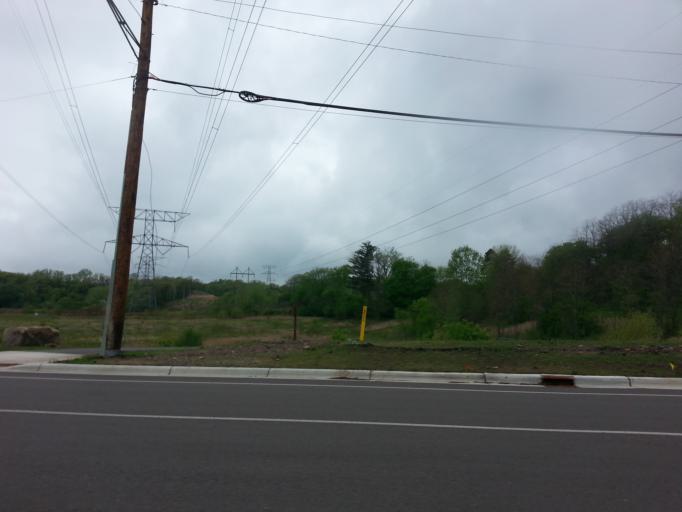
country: US
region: Minnesota
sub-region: Washington County
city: Oak Park Heights
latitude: 45.0302
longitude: -92.7911
